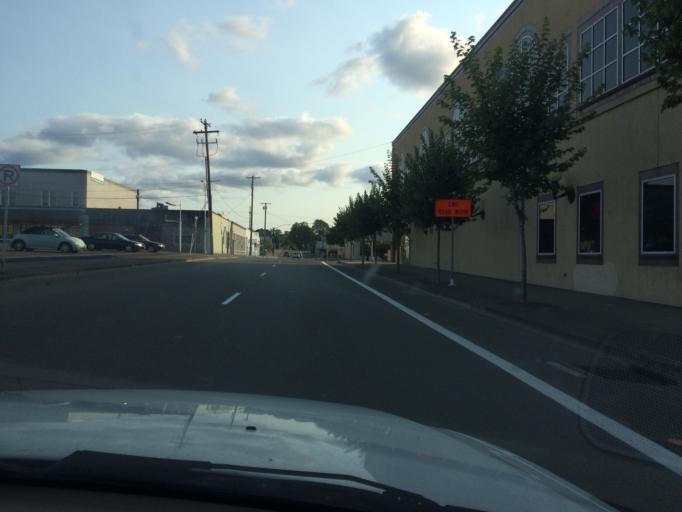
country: US
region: Oregon
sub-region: Douglas County
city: Roseburg
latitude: 43.2096
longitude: -123.3472
